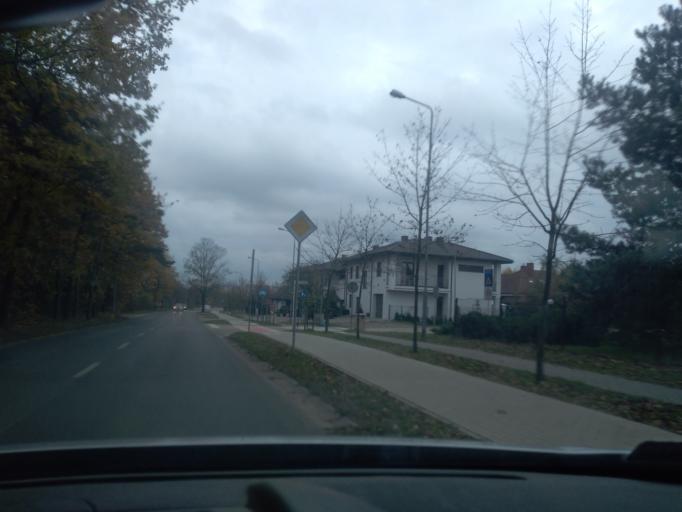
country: PL
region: Greater Poland Voivodeship
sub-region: Powiat poznanski
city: Suchy Las
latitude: 52.4726
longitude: 16.8996
